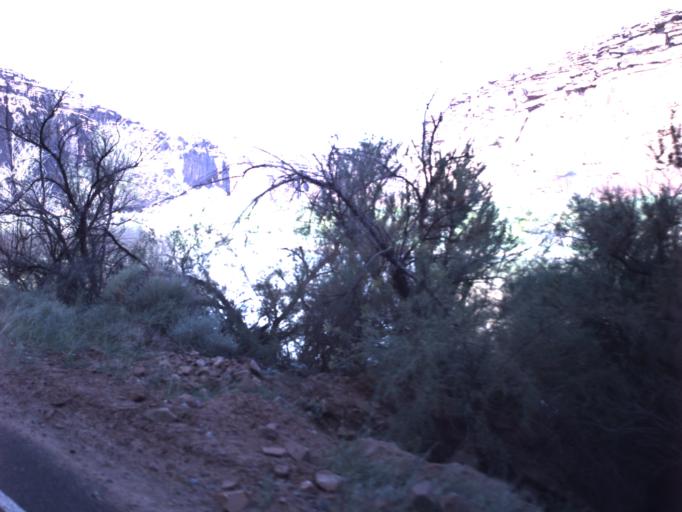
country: US
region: Utah
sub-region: Grand County
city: Moab
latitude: 38.5587
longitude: -109.6567
